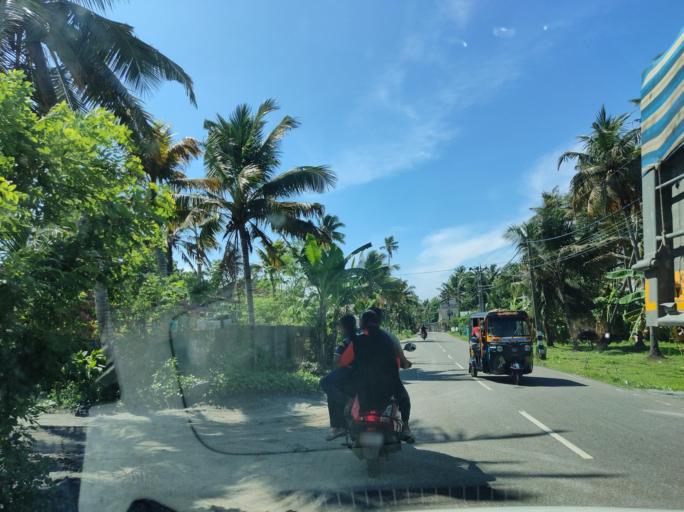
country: IN
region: Kerala
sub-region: Alappuzha
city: Kayankulam
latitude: 9.1827
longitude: 76.4425
